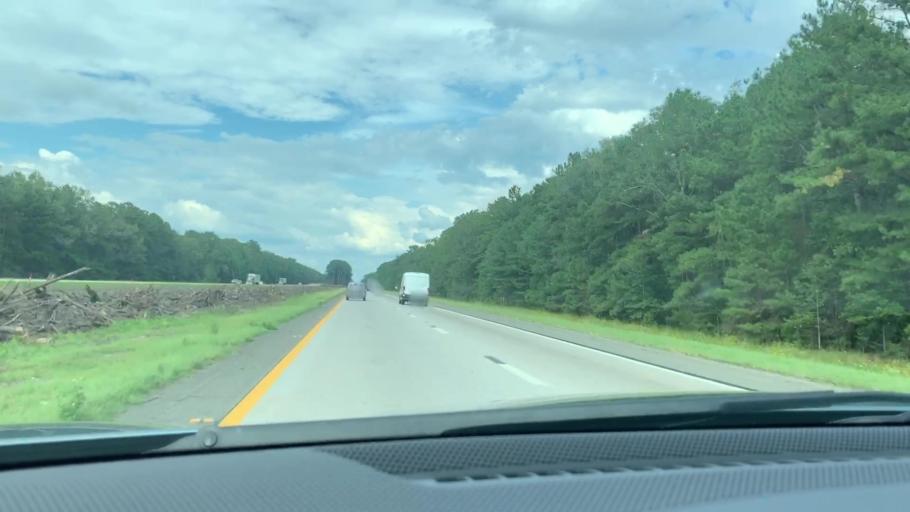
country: US
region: South Carolina
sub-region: Jasper County
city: Hardeeville
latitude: 32.3690
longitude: -81.0340
